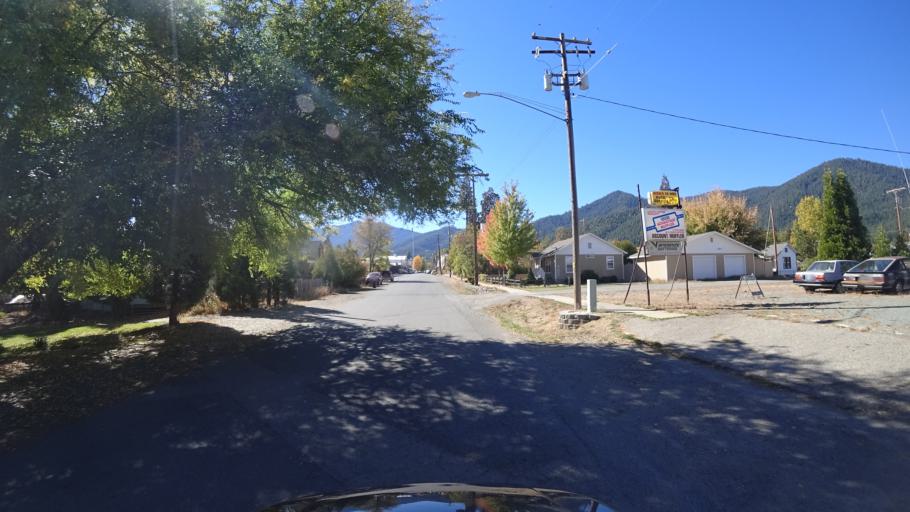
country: US
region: California
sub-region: Siskiyou County
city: Yreka
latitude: 41.4578
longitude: -122.8916
